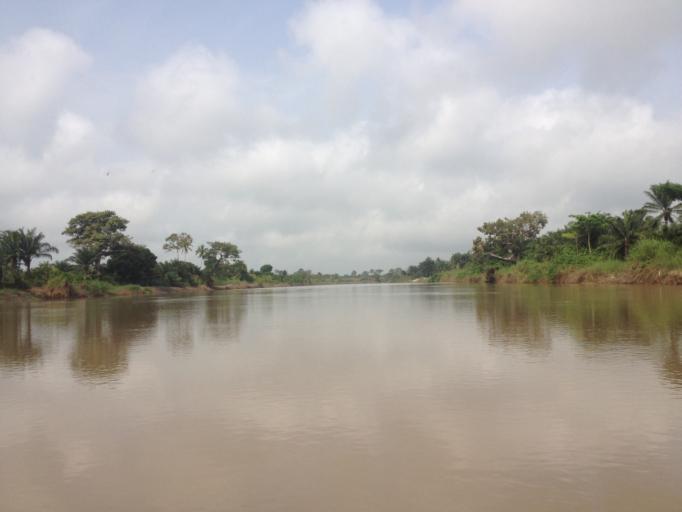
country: BJ
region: Mono
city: Come
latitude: 6.3841
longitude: 1.7804
